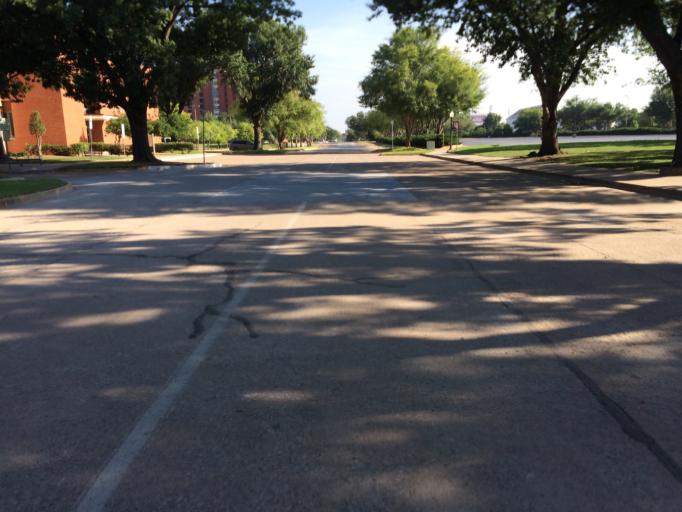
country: US
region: Oklahoma
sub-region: Cleveland County
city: Norman
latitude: 35.1976
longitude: -97.4442
